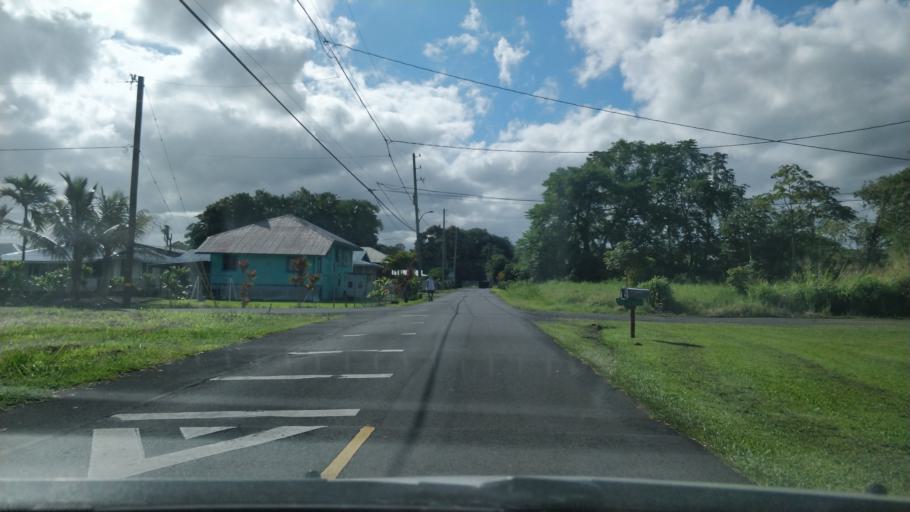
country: US
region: Hawaii
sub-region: Hawaii County
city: Hilo
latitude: 19.6672
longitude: -155.1054
